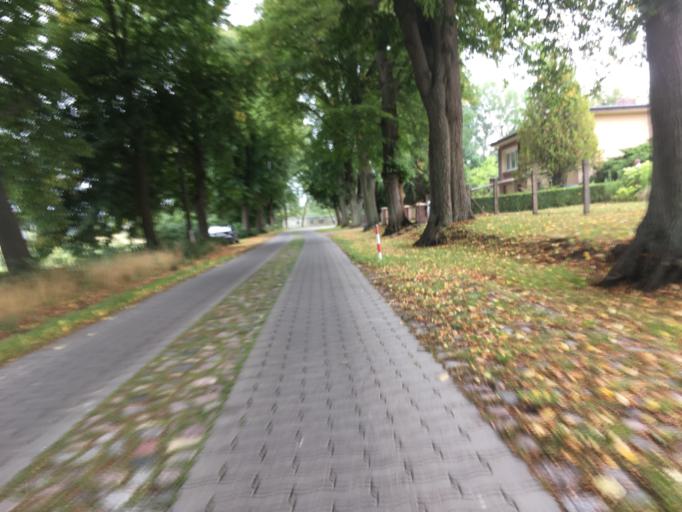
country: DE
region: Brandenburg
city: Passow
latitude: 53.1513
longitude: 14.1032
